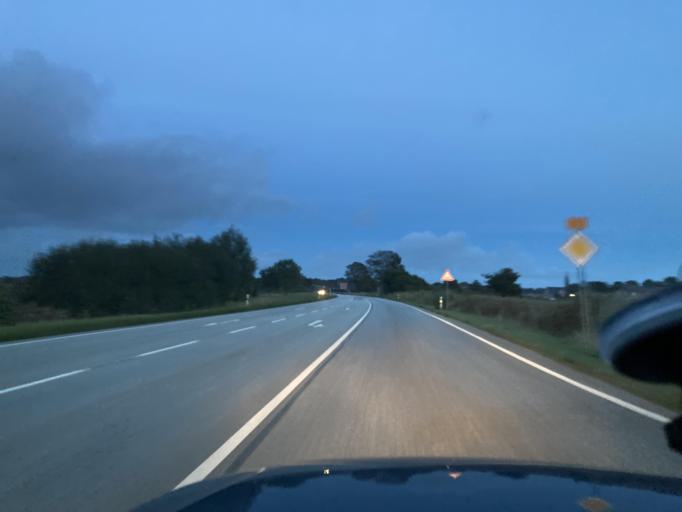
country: DE
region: Schleswig-Holstein
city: Kotzenbull
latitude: 54.3257
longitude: 8.9224
